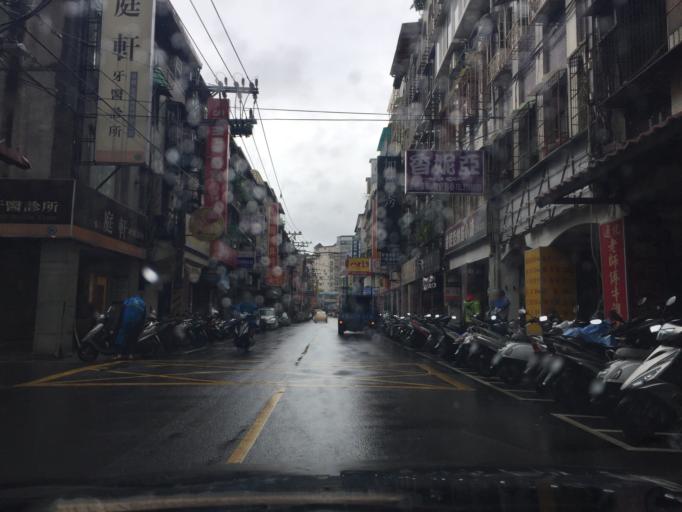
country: TW
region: Taipei
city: Taipei
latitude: 25.0796
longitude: 121.5934
